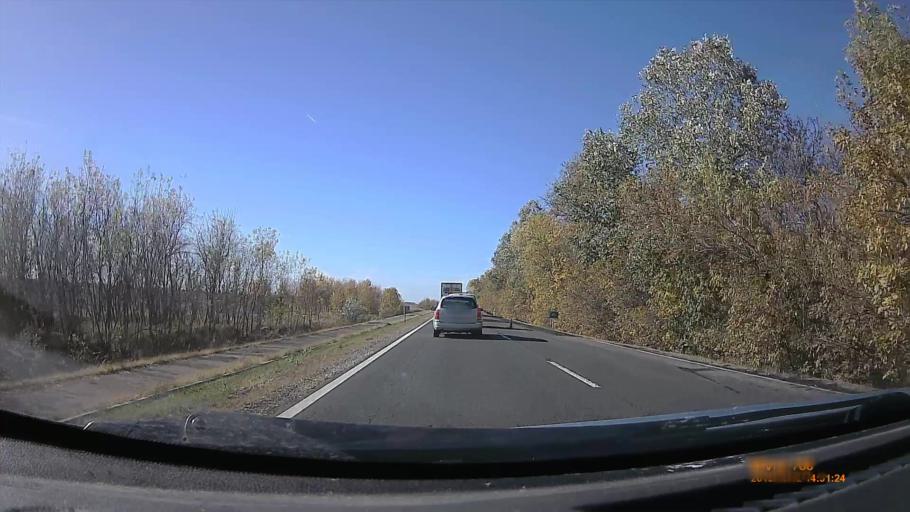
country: HU
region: Hajdu-Bihar
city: Berettyoujfalu
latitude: 47.1771
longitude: 21.5921
